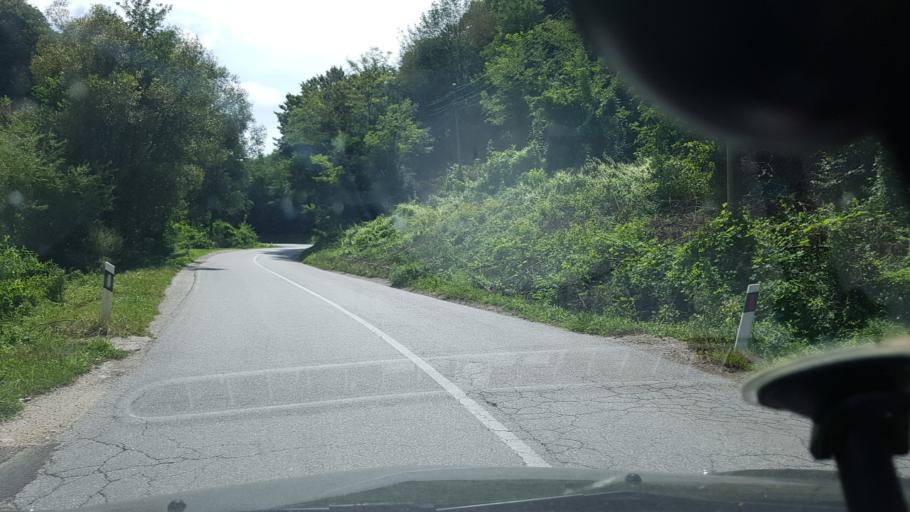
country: HR
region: Krapinsko-Zagorska
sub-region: Grad Krapina
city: Krapina
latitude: 46.1904
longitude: 15.8577
